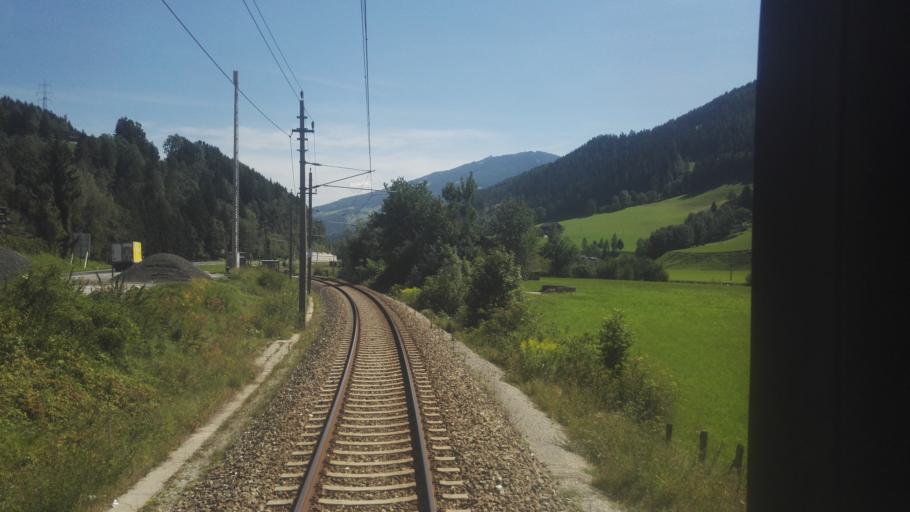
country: AT
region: Styria
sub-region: Politischer Bezirk Liezen
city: Schladming
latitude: 47.3886
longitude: 13.6208
